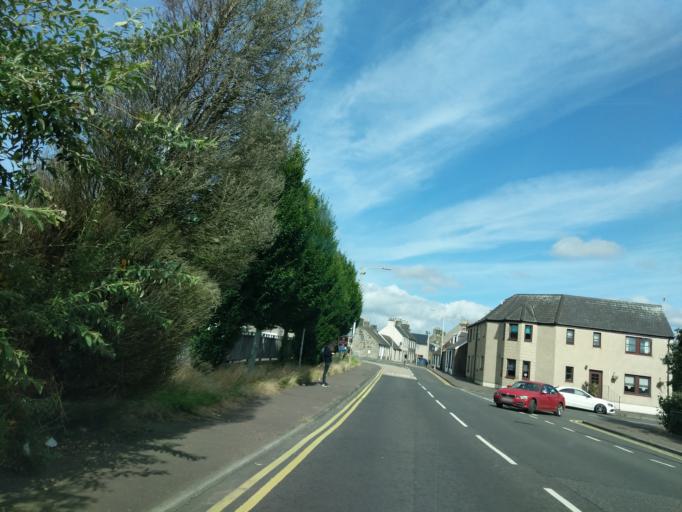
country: GB
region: Scotland
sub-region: Perth and Kinross
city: Kinross
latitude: 56.1990
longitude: -3.4228
